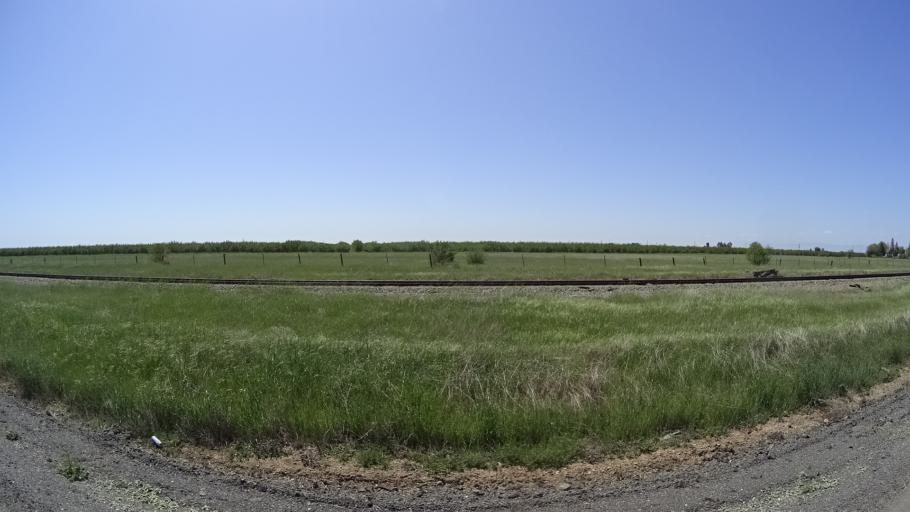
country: US
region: California
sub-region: Glenn County
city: Hamilton City
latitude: 39.7680
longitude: -122.1033
